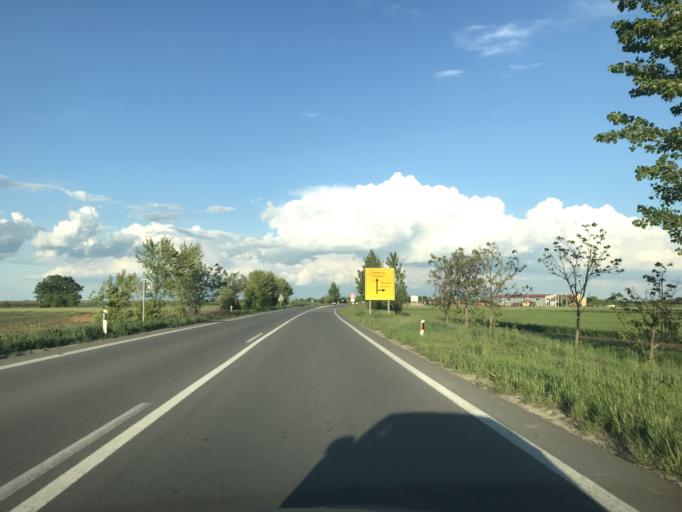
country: RS
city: Aradac
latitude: 45.3922
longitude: 20.2933
